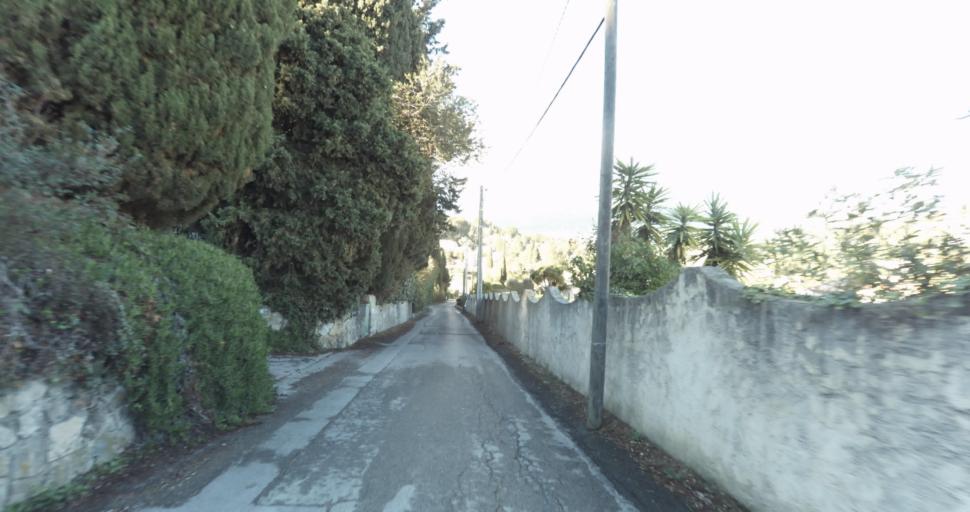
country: FR
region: Provence-Alpes-Cote d'Azur
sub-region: Departement des Alpes-Maritimes
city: Saint-Paul-de-Vence
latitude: 43.6994
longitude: 7.1356
